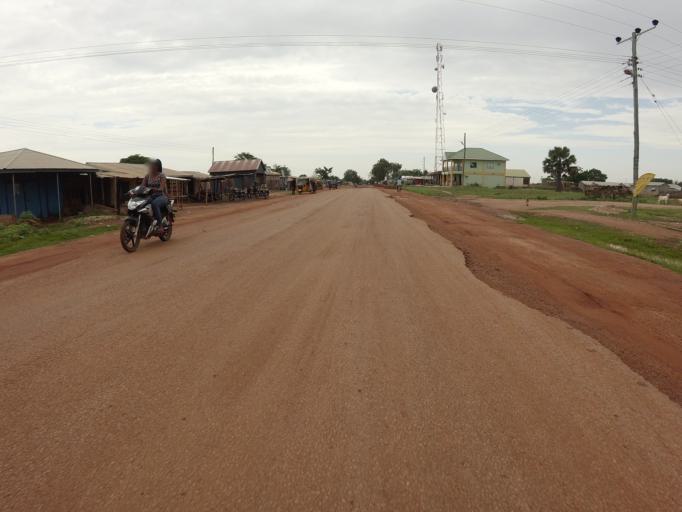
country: GH
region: Upper East
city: Bawku
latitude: 10.9366
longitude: -0.4932
